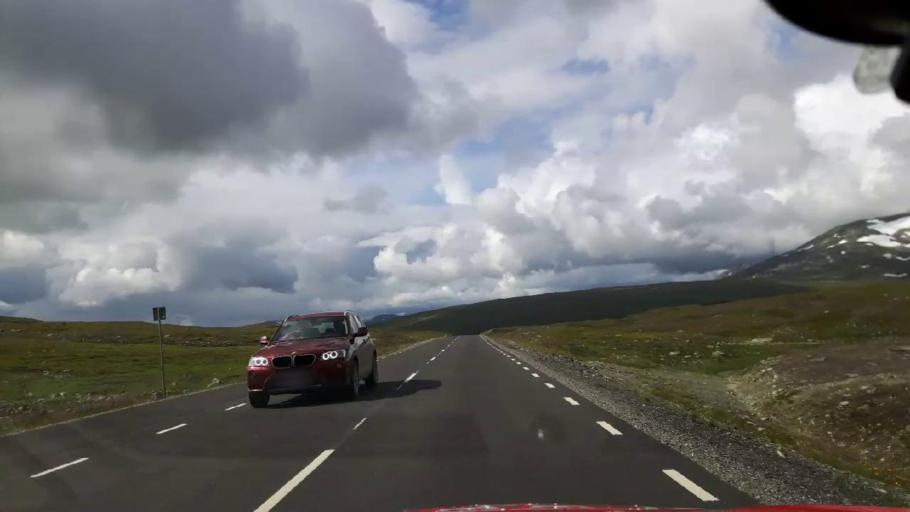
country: NO
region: Nordland
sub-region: Hattfjelldal
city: Hattfjelldal
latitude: 65.0575
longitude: 14.3658
